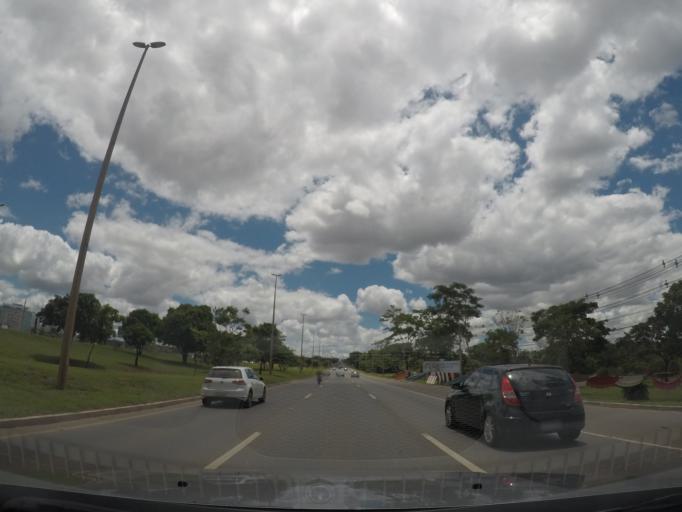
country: BR
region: Federal District
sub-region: Brasilia
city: Brasilia
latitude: -15.7368
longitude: -47.9151
